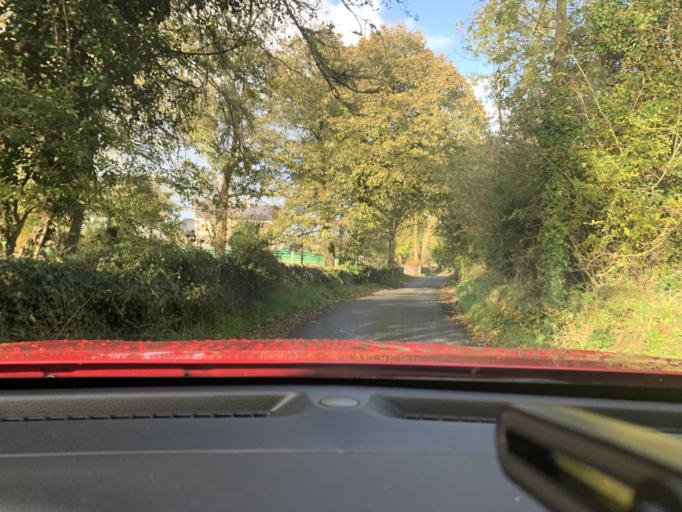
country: IE
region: Connaught
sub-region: Sligo
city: Ballymote
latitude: 54.1027
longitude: -8.4341
